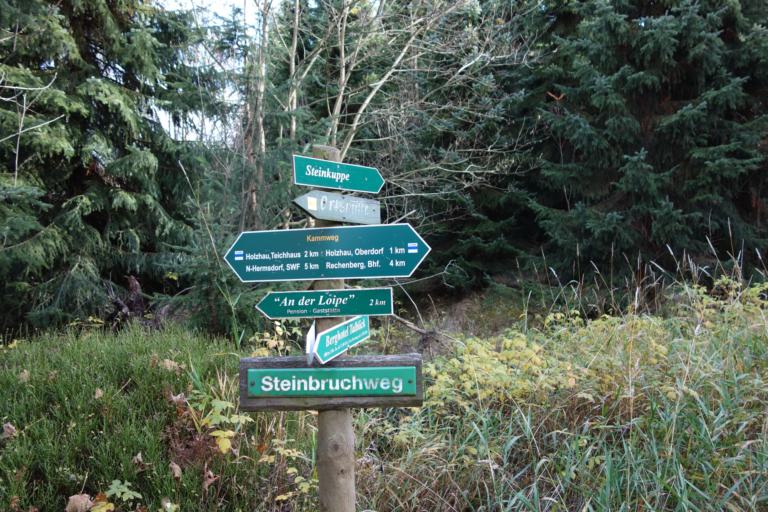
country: DE
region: Saxony
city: Rechenberg-Bienenmuhle
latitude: 50.7206
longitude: 13.5976
